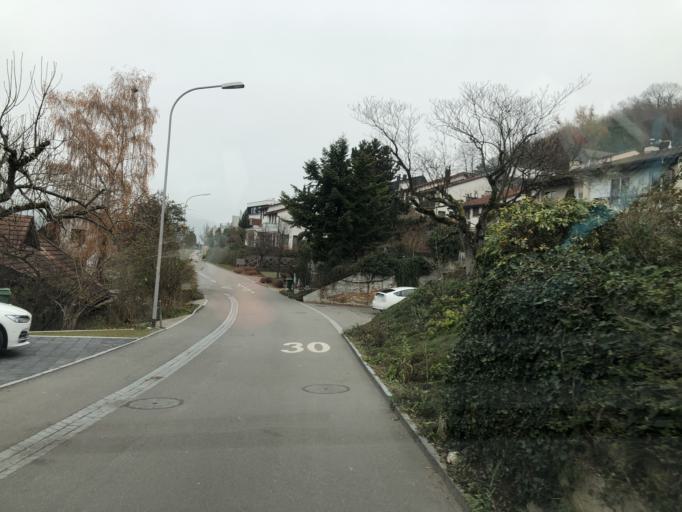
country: CH
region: Aargau
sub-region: Bezirk Baden
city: Gebenstorf
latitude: 47.4812
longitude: 8.2453
